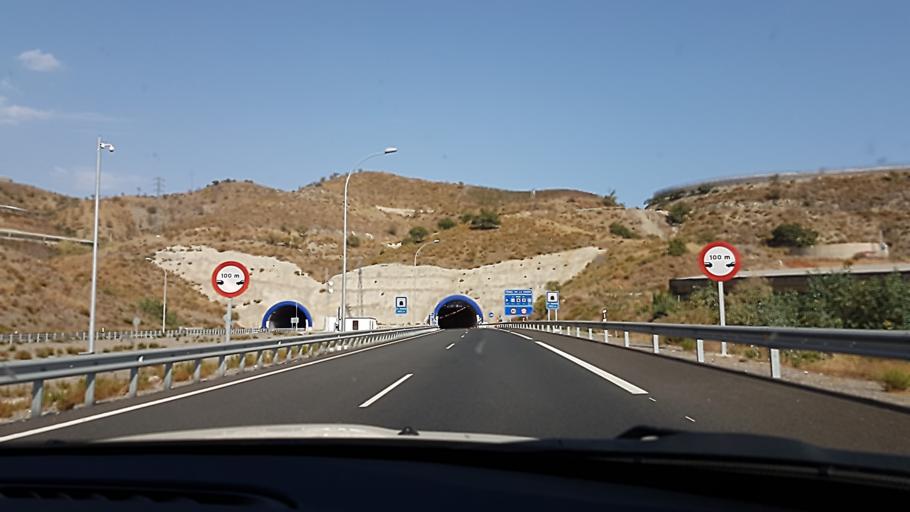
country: ES
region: Andalusia
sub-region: Provincia de Granada
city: Polopos
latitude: 36.7505
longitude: -3.3025
